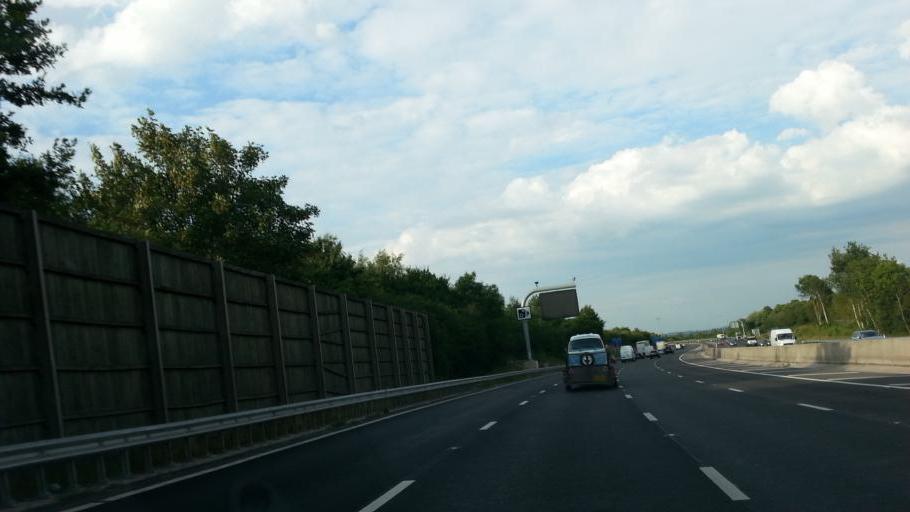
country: GB
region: England
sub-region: Worcestershire
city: Droitwich
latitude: 52.2675
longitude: -2.1332
